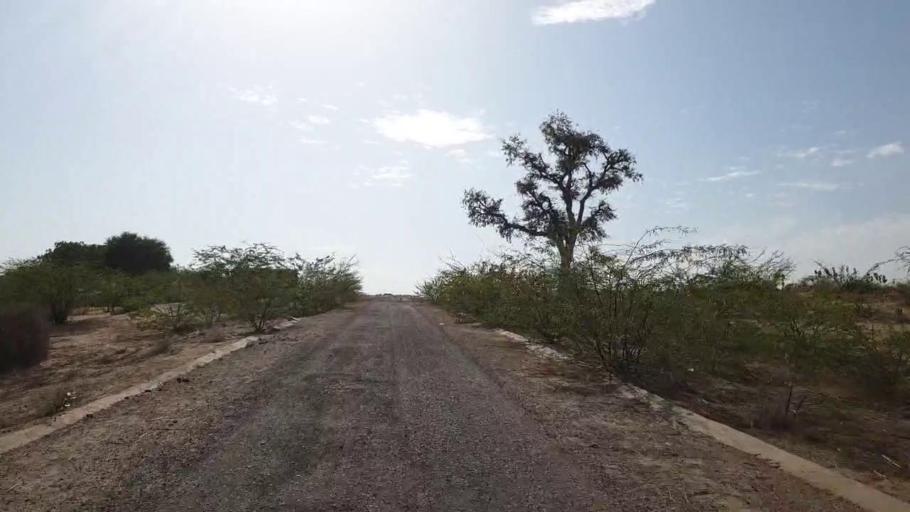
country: PK
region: Sindh
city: Islamkot
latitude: 25.0643
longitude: 70.0384
